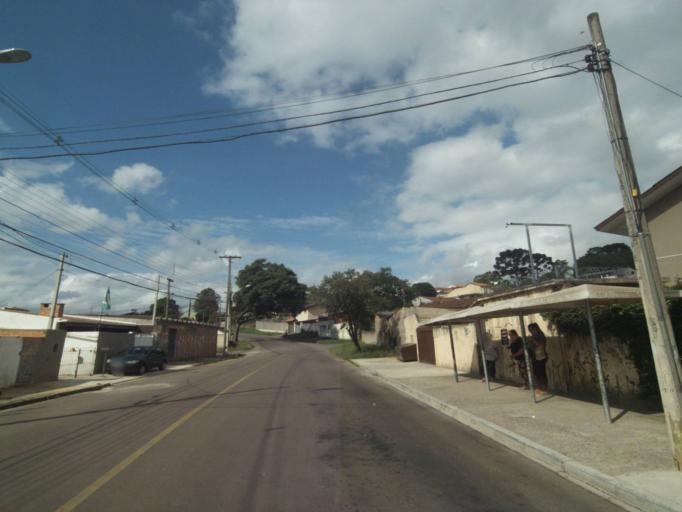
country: BR
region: Parana
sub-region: Curitiba
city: Curitiba
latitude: -25.3817
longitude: -49.3009
